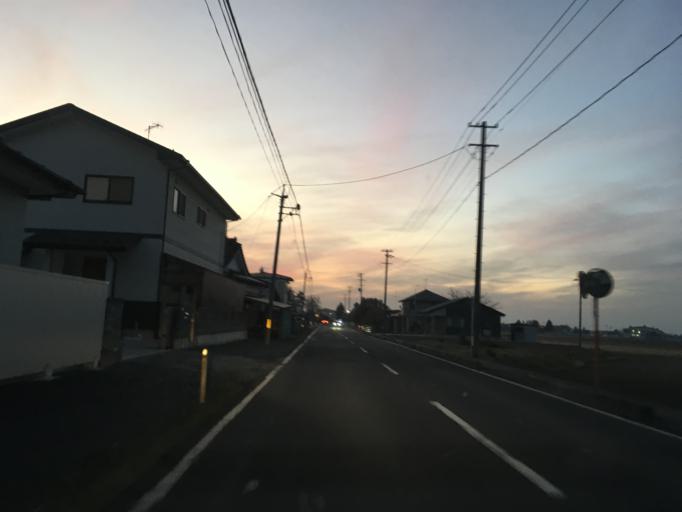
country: JP
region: Miyagi
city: Wakuya
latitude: 38.7126
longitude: 141.2282
